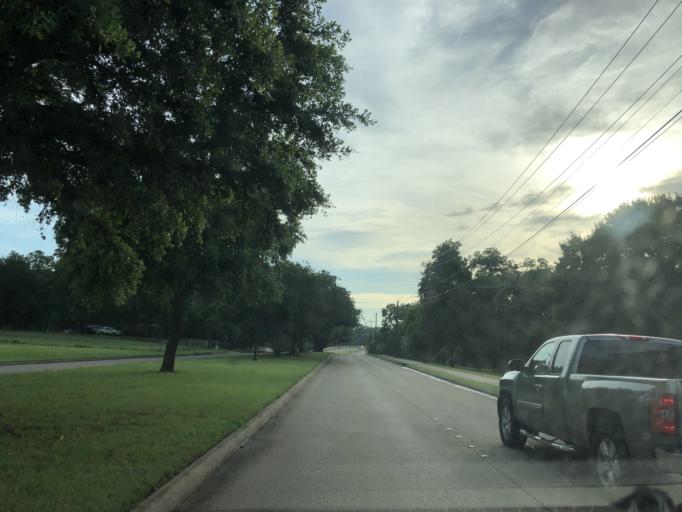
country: US
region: Texas
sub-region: Dallas County
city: Garland
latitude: 32.8483
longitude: -96.6166
